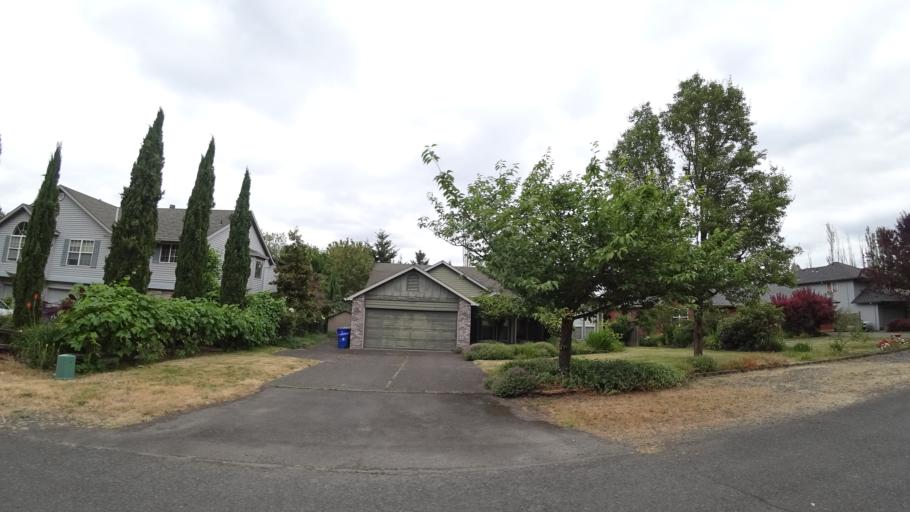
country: US
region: Washington
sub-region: Clark County
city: Vancouver
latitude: 45.5941
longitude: -122.6568
